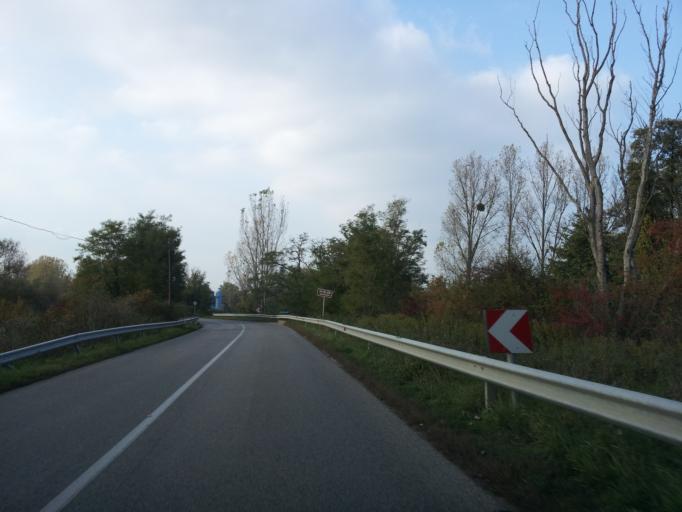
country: HU
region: Komarom-Esztergom
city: Bokod
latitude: 47.4847
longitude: 18.2727
